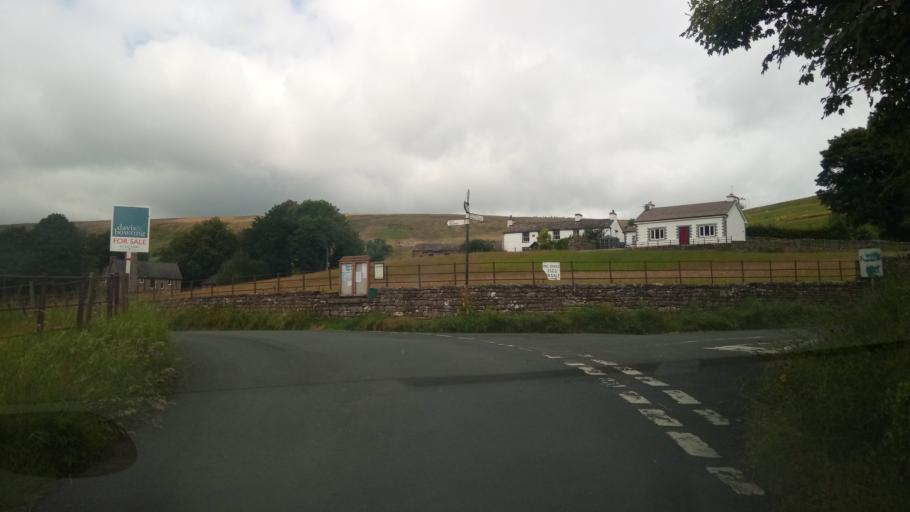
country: GB
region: England
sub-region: North Yorkshire
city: Ingleton
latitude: 54.2773
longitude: -2.3690
